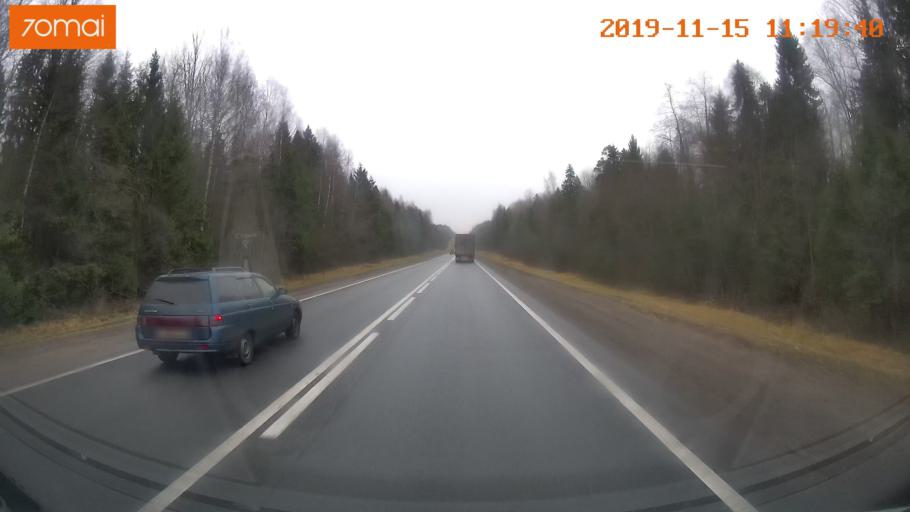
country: RU
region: Vologda
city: Molochnoye
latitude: 59.1392
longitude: 39.2971
